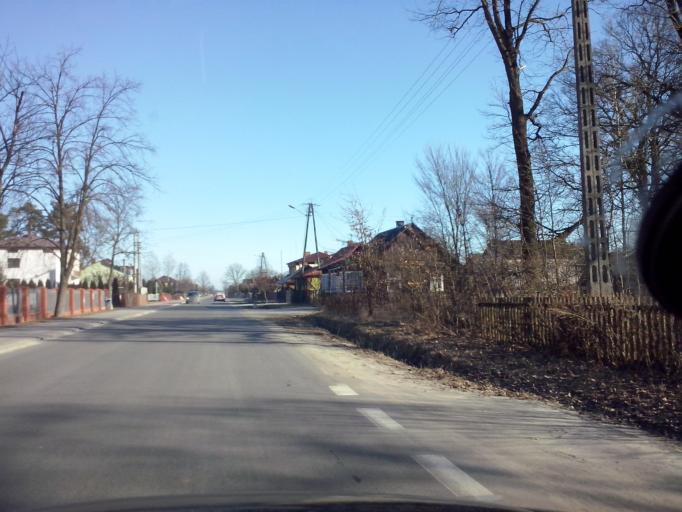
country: PL
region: Subcarpathian Voivodeship
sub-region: Powiat nizanski
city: Harasiuki
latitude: 50.4743
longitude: 22.4773
